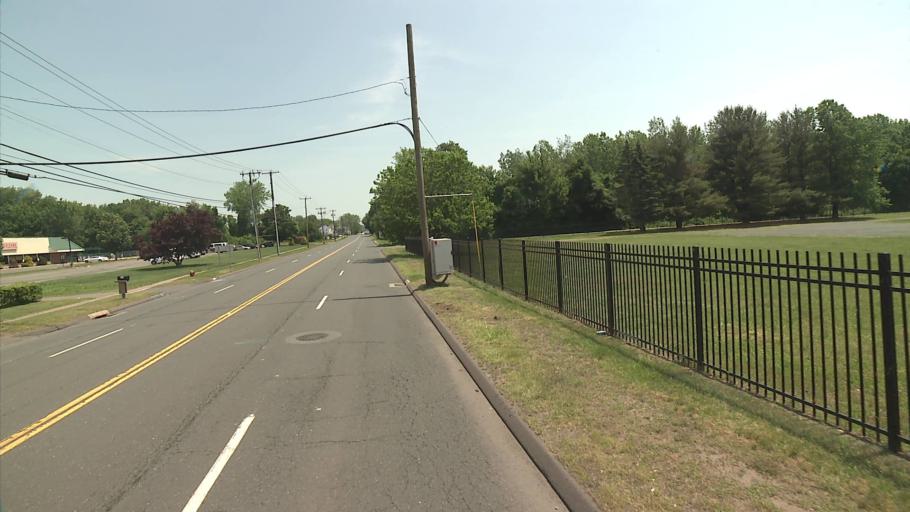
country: US
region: Connecticut
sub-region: Hartford County
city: East Hartford
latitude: 41.7634
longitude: -72.6164
